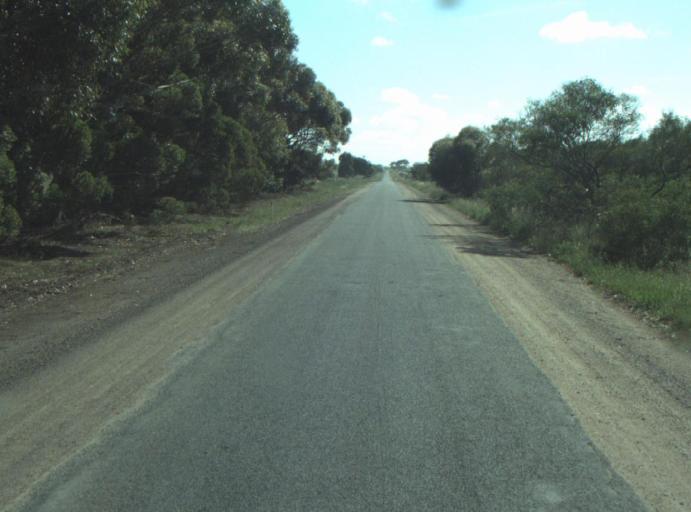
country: AU
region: Victoria
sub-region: Greater Geelong
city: Lara
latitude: -37.9984
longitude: 144.4446
